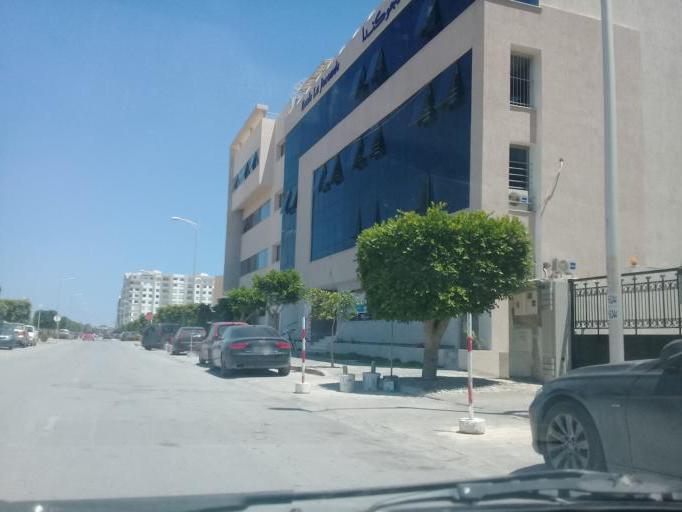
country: TN
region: Tunis
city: La Goulette
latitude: 36.8438
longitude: 10.2773
